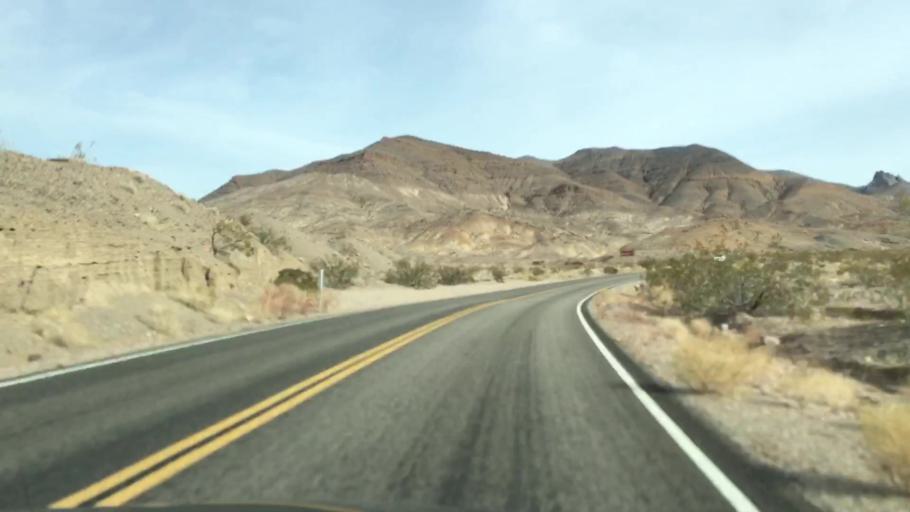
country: US
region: Nevada
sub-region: Nye County
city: Beatty
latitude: 36.7342
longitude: -116.9721
